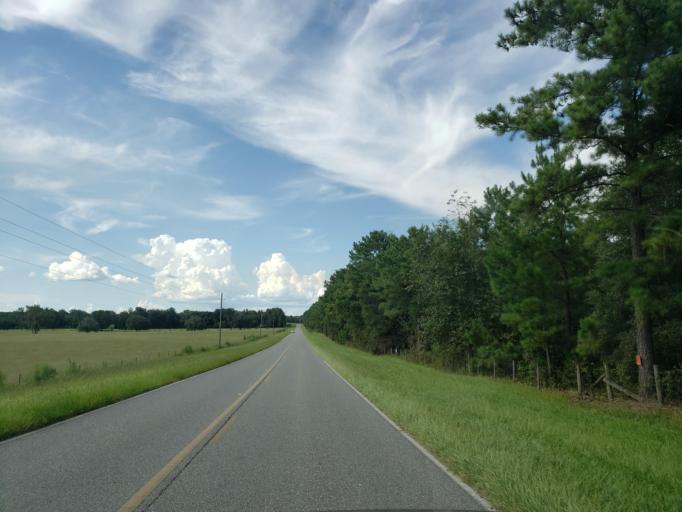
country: US
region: Florida
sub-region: Madison County
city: Madison
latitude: 30.5895
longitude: -83.2243
